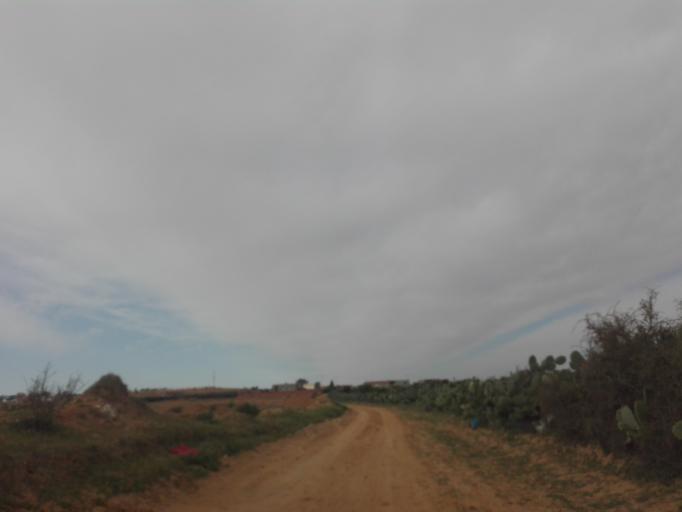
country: TN
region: Safaqis
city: Sfax
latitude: 34.7344
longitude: 10.4998
